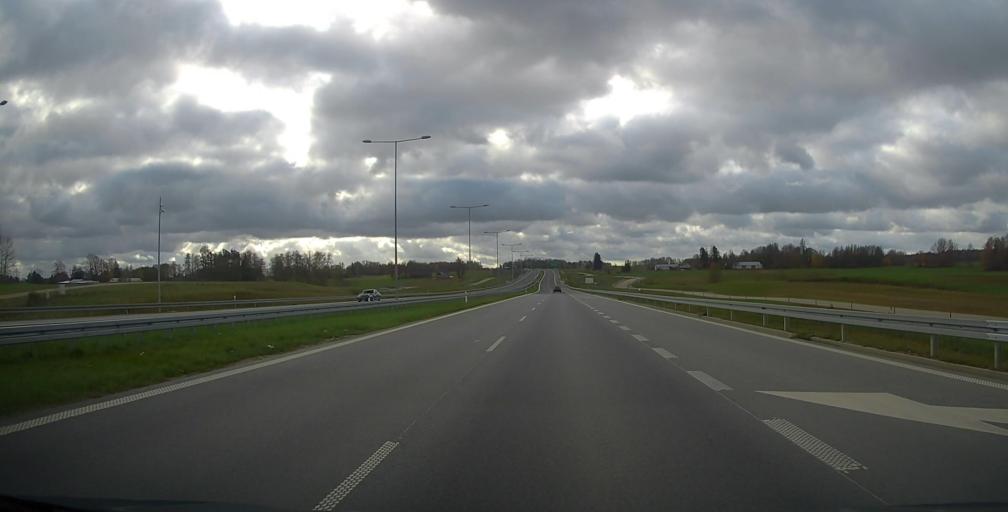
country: PL
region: Podlasie
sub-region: Powiat suwalski
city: Raczki
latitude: 53.9673
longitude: 22.7810
